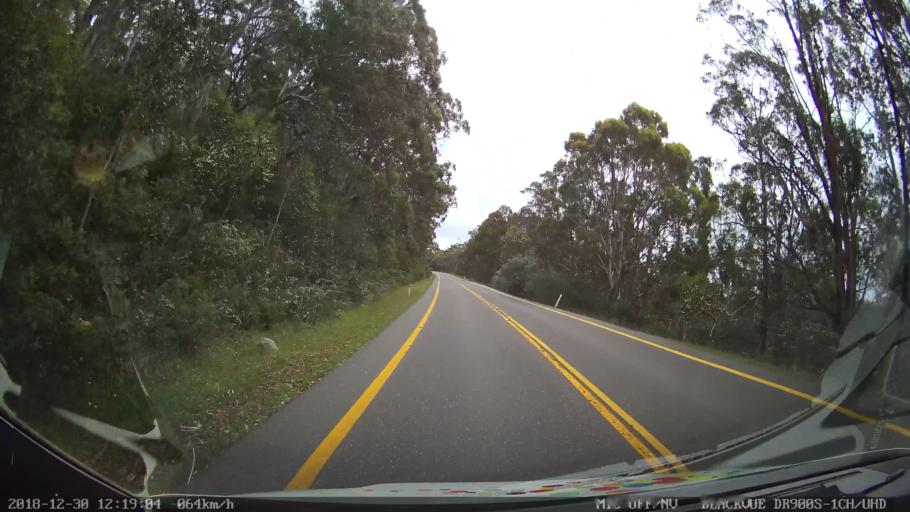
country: AU
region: New South Wales
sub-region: Snowy River
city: Jindabyne
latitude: -36.3478
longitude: 148.5447
